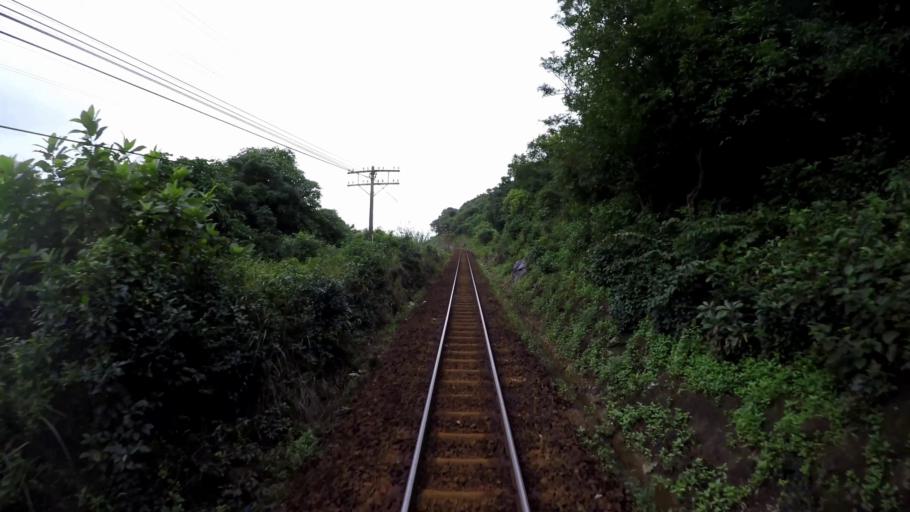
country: VN
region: Da Nang
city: Lien Chieu
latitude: 16.2076
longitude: 108.1229
